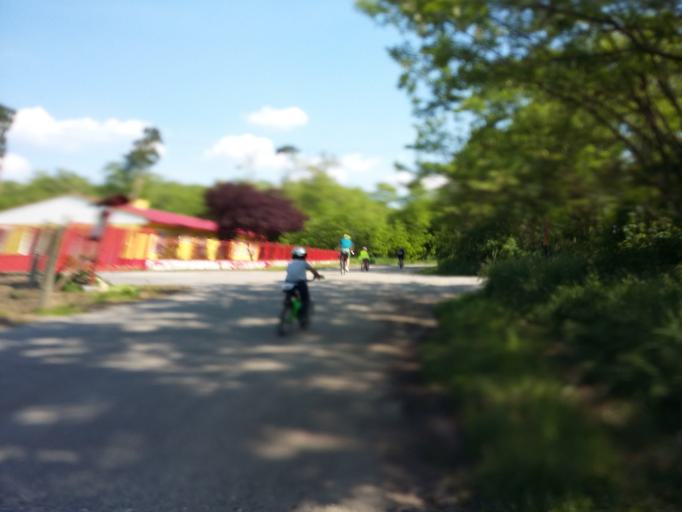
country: AT
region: Lower Austria
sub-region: Politischer Bezirk Ganserndorf
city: Drosing
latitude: 48.5078
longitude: 16.9645
